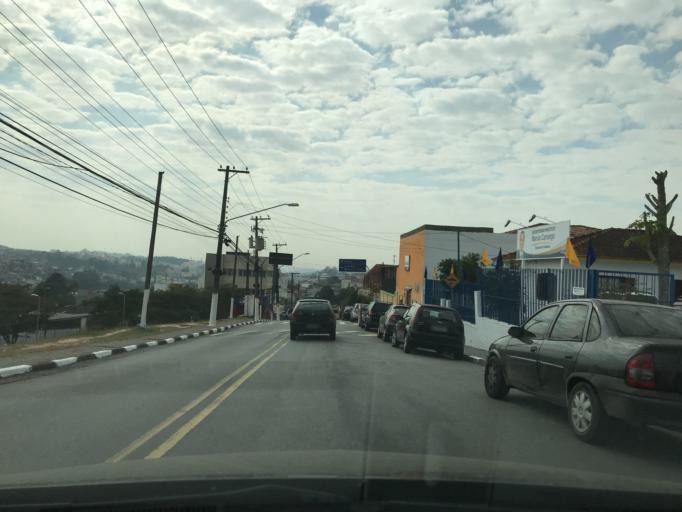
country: BR
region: Sao Paulo
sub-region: Cotia
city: Cotia
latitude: -23.6066
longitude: -46.9146
